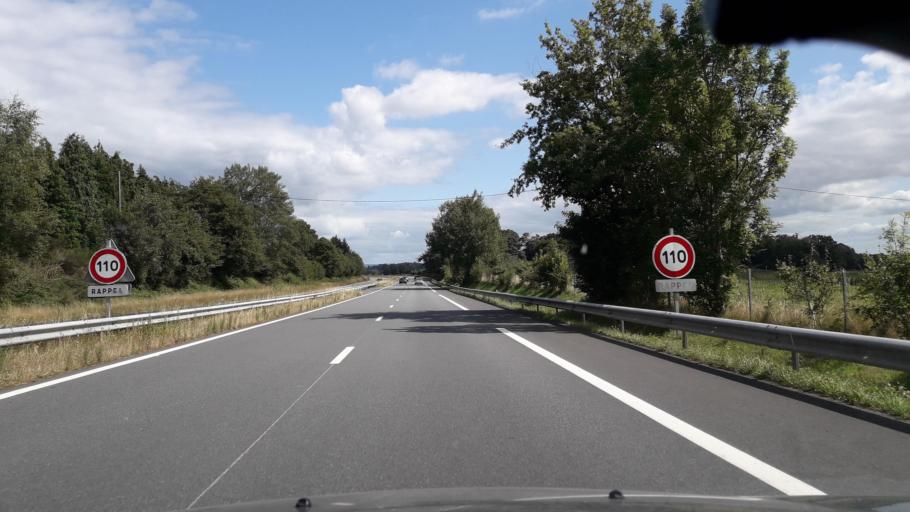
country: FR
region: Limousin
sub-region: Departement de la Creuse
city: Le Grand-Bourg
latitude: 46.2160
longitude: 1.6337
